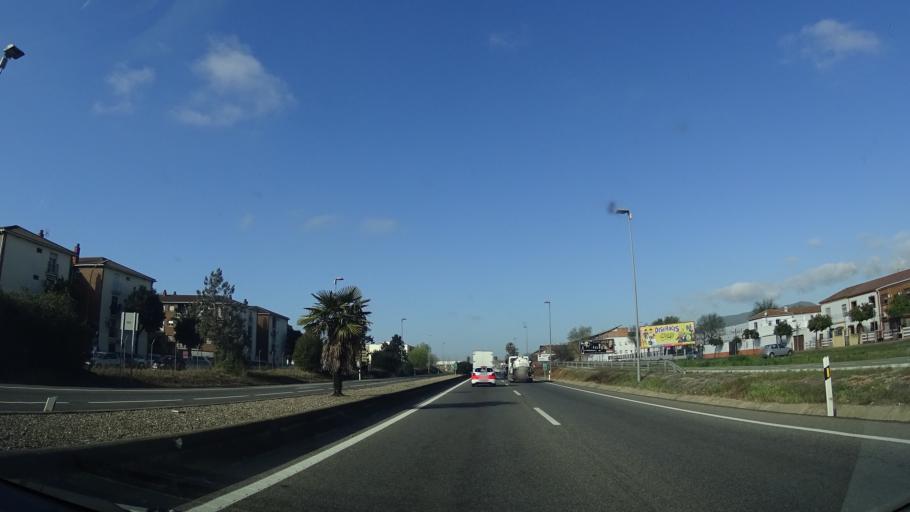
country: ES
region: Andalusia
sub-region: Province of Cordoba
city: Cordoba
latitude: 37.8814
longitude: -4.8173
